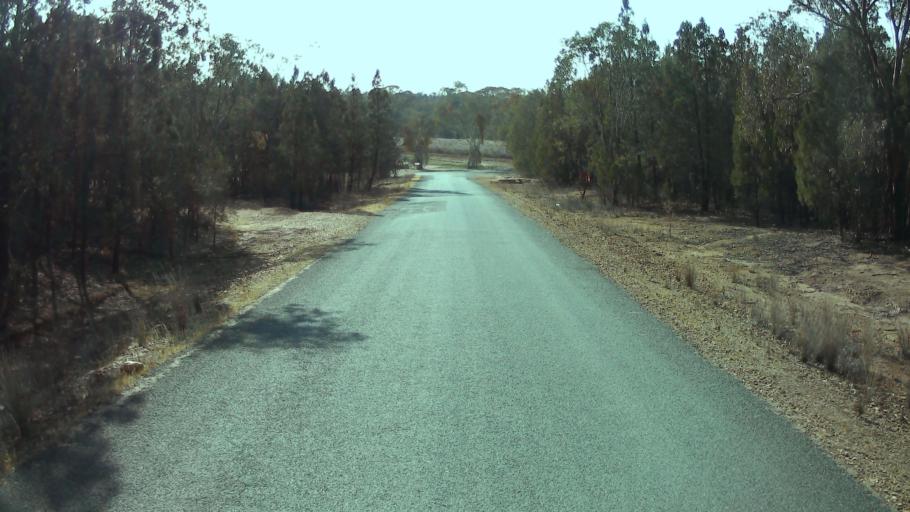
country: AU
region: New South Wales
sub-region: Weddin
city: Grenfell
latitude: -33.8835
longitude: 148.1517
